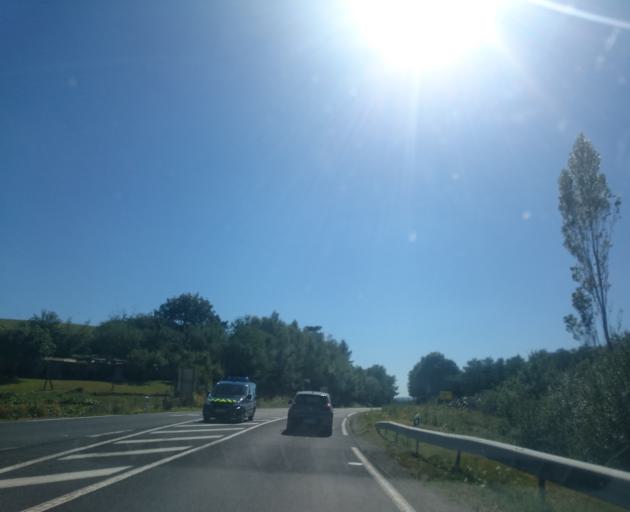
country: FR
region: Auvergne
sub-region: Departement du Cantal
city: Saint-Mamet-la-Salvetat
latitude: 44.8584
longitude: 2.2908
